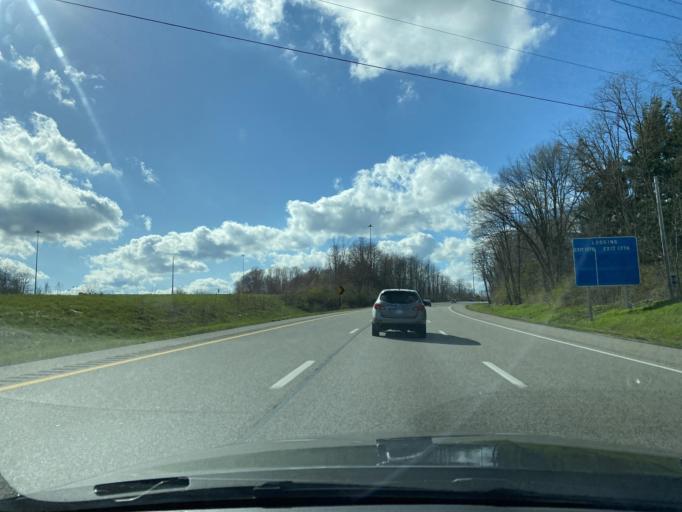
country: US
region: Ohio
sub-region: Summit County
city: Montrose-Ghent
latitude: 41.1201
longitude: -81.6479
